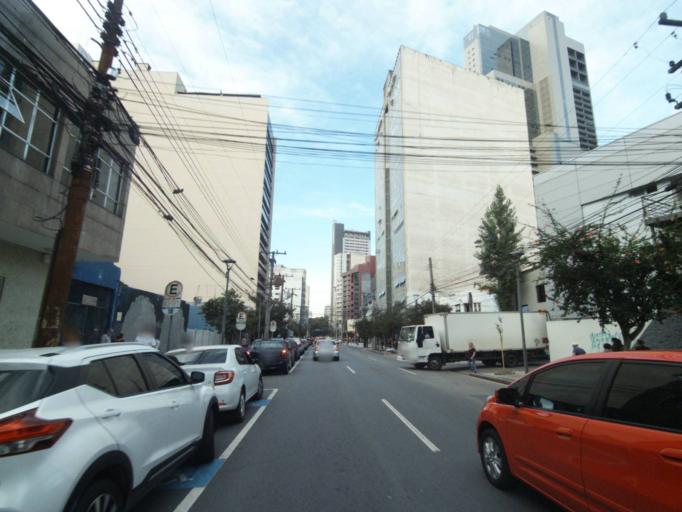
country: BR
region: Parana
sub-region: Curitiba
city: Curitiba
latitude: -25.4346
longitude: -49.2804
